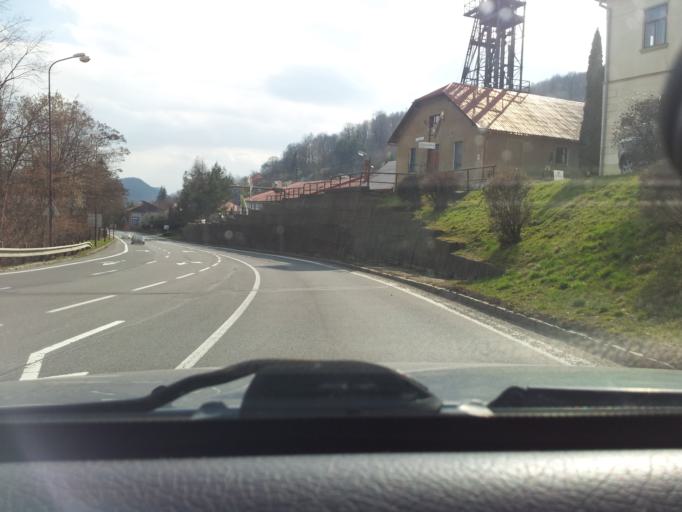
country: SK
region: Banskobystricky
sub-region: Okres Ziar nad Hronom
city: Kremnica
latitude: 48.7080
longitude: 18.9145
